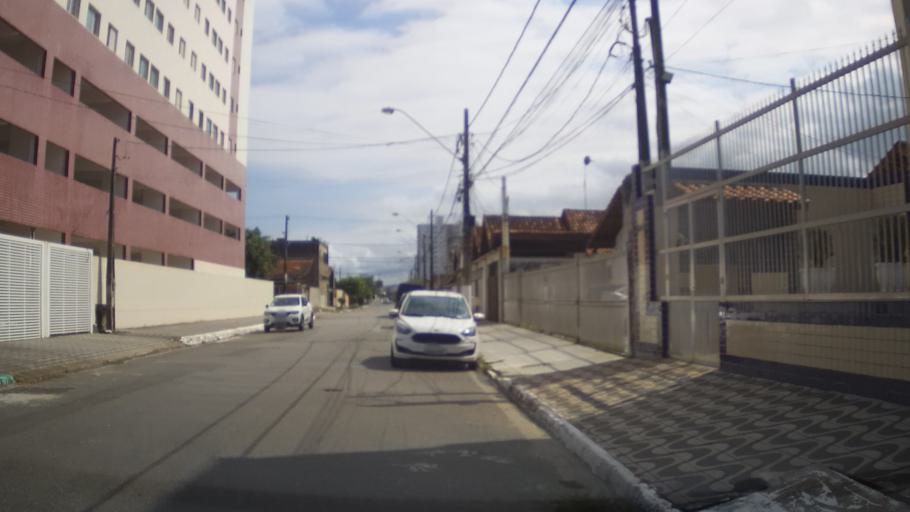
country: BR
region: Sao Paulo
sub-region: Praia Grande
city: Praia Grande
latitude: -24.0155
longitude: -46.4546
